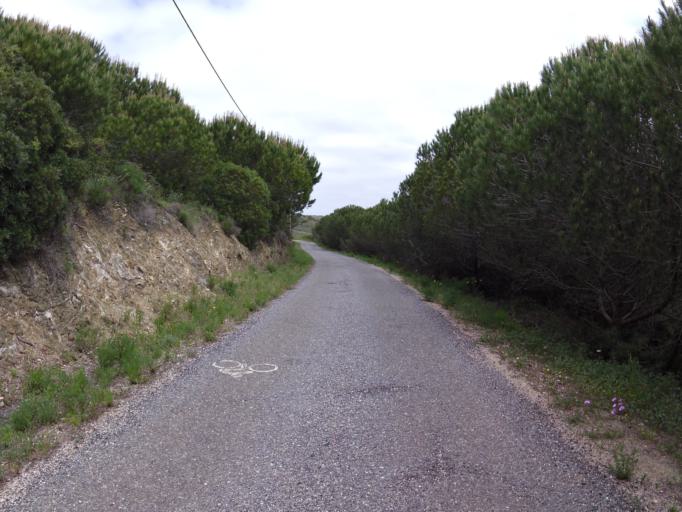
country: PT
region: Faro
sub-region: Vila do Bispo
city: Vila do Bispo
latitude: 37.0741
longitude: -8.8750
